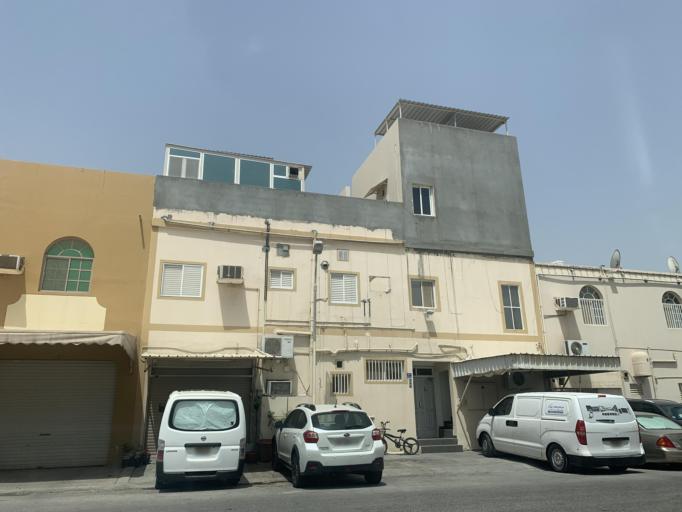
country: BH
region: Northern
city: Madinat `Isa
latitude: 26.1491
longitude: 50.5262
